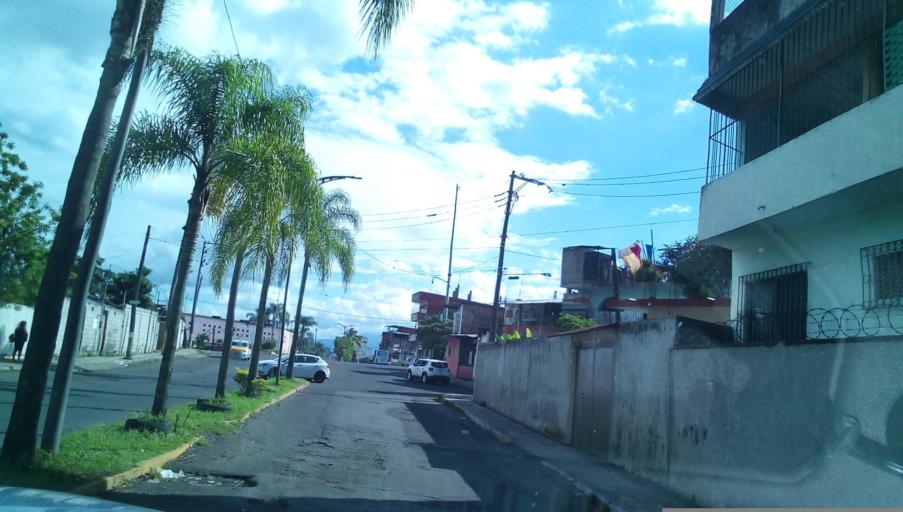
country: MX
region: Veracruz
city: Cordoba
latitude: 18.8877
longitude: -96.9222
